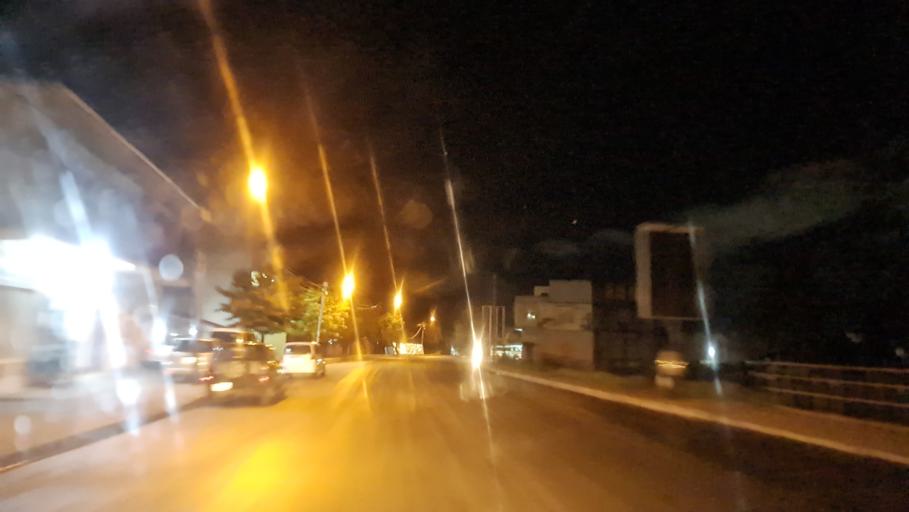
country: MZ
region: Nampula
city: Nampula
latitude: -15.1137
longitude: 39.2826
